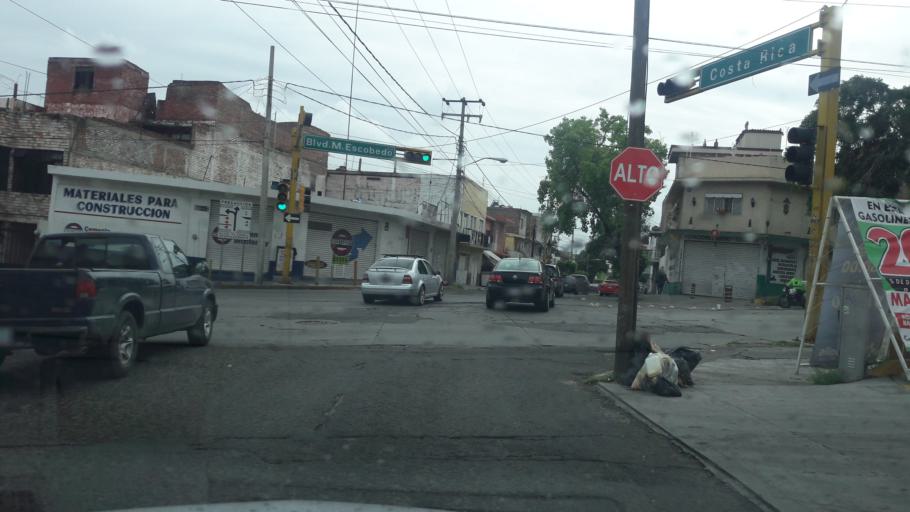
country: MX
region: Guanajuato
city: Leon
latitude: 21.1168
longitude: -101.6900
